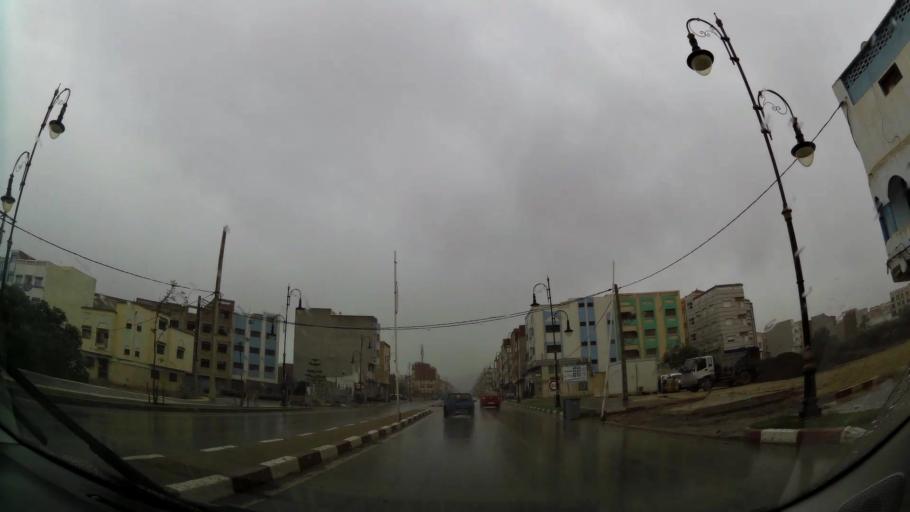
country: MA
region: Taza-Al Hoceima-Taounate
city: Imzourene
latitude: 35.1094
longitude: -3.8414
